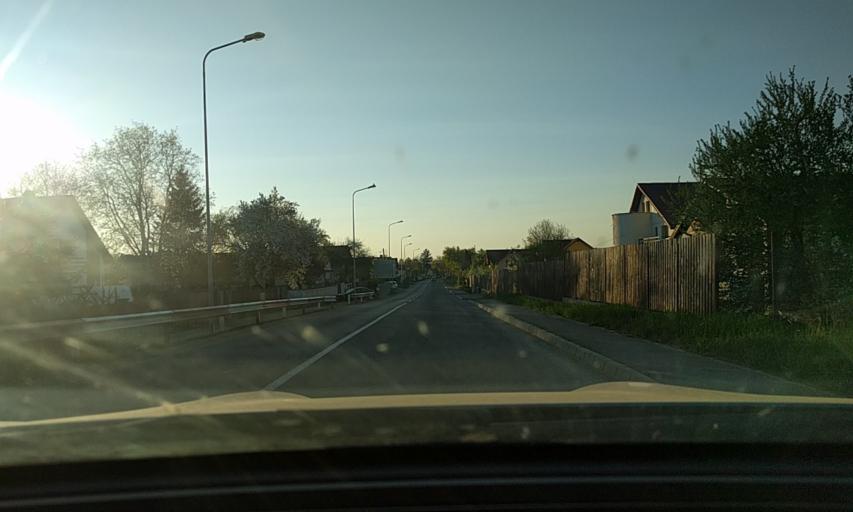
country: RO
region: Brasov
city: Brasov
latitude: 45.6918
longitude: 25.5649
